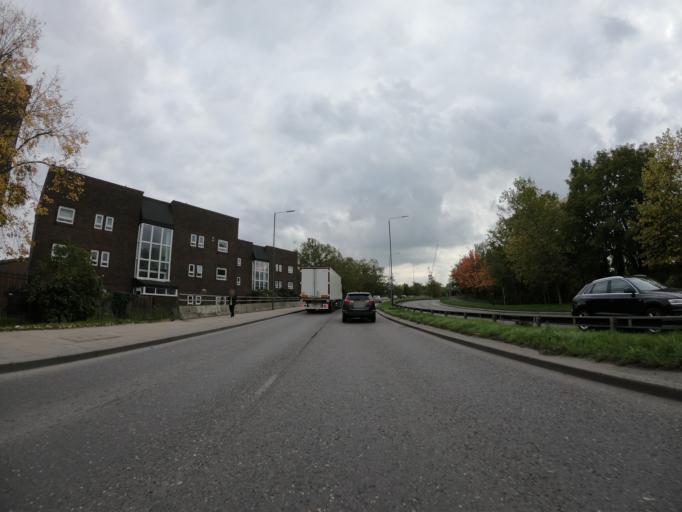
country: GB
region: England
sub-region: Greater London
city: Erith
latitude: 51.4772
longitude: 0.1809
